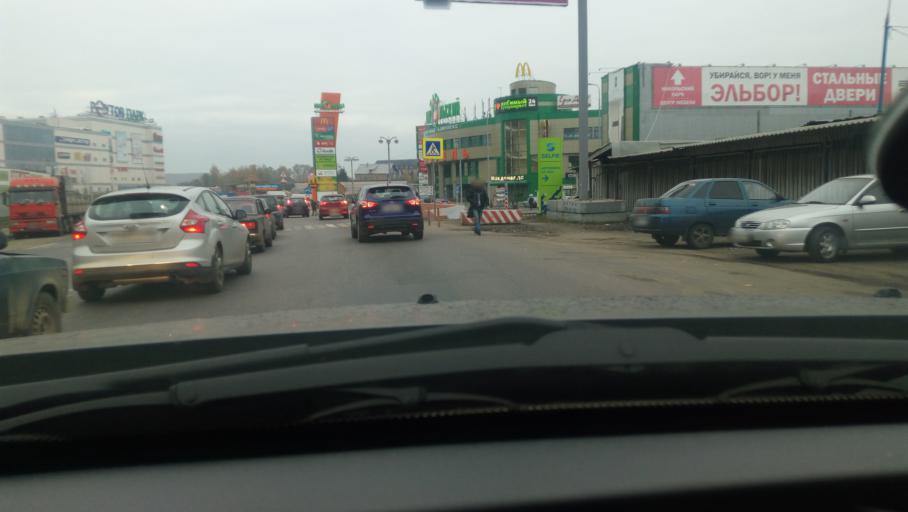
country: RU
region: Moskovskaya
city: Reutov
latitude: 55.7496
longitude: 37.8849
